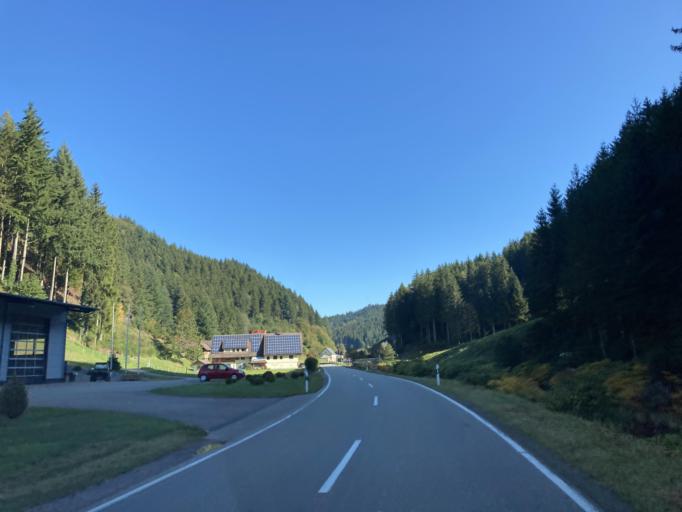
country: DE
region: Baden-Wuerttemberg
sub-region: Freiburg Region
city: Oberwolfach
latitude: 48.3608
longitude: 8.2706
